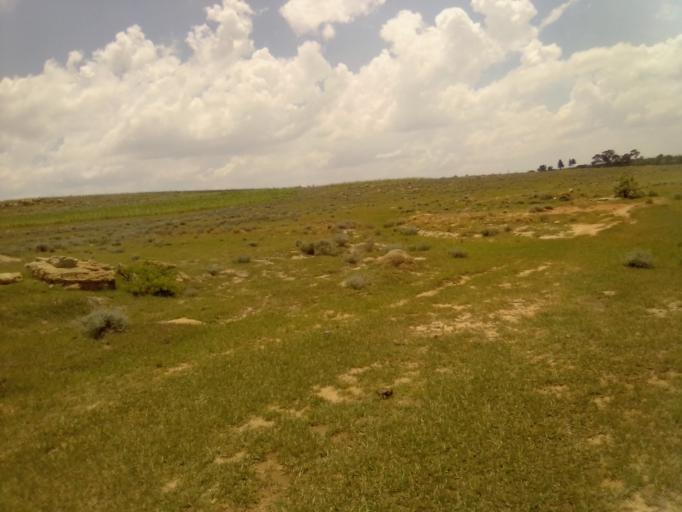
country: LS
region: Maseru
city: Maseru
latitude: -29.4576
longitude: 27.5615
